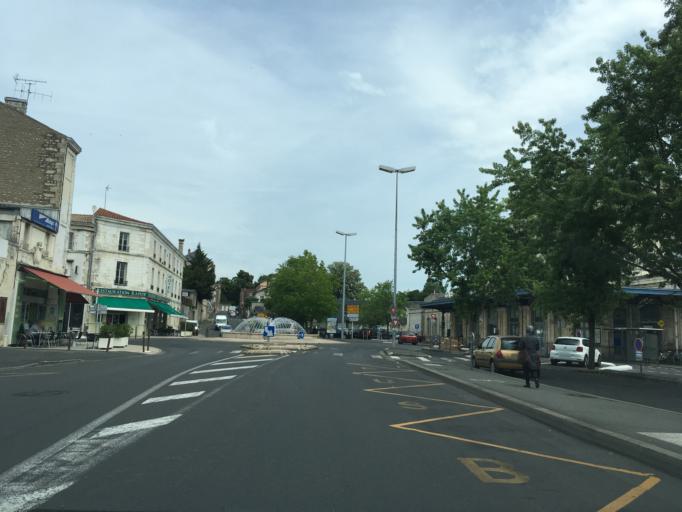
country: FR
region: Poitou-Charentes
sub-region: Departement des Deux-Sevres
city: Niort
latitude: 46.3192
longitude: -0.4554
